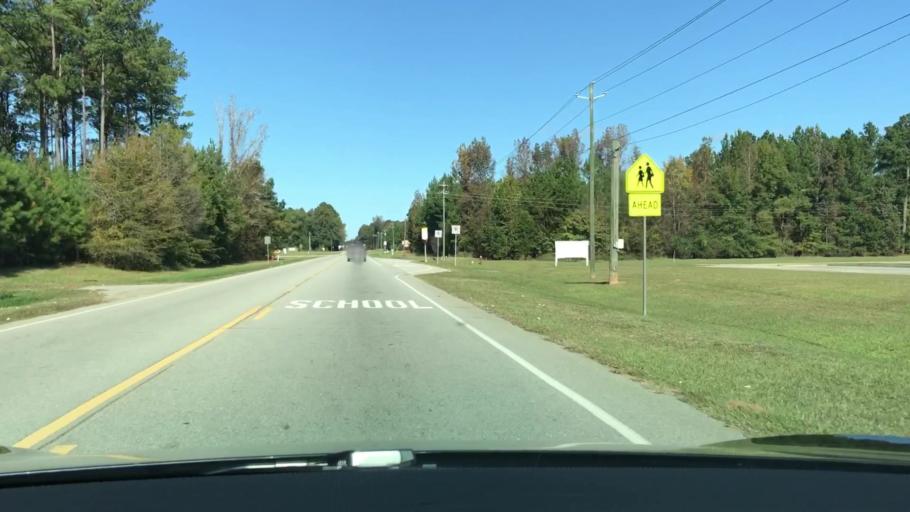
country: US
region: Georgia
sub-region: Warren County
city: West Warrenton
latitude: 33.4156
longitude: -82.6772
